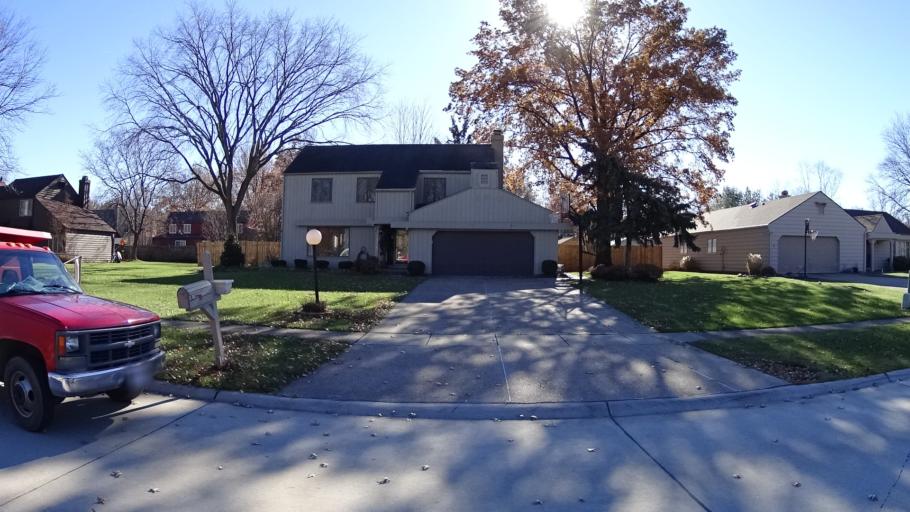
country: US
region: Ohio
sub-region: Lorain County
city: Avon Lake
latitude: 41.4942
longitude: -82.0139
